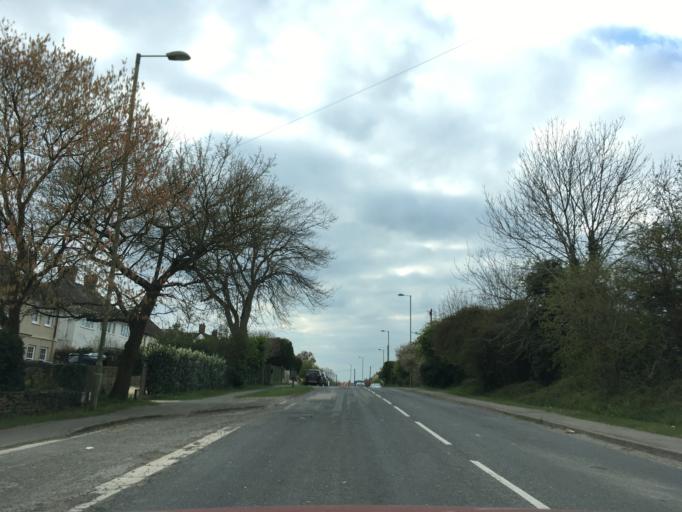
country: GB
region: England
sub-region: Oxfordshire
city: Witney
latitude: 51.7903
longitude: -1.4953
